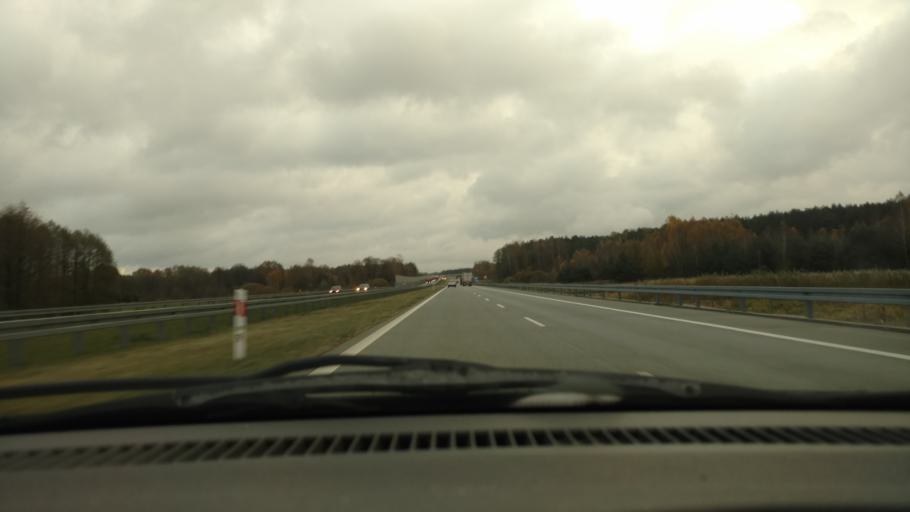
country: PL
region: Lodz Voivodeship
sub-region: Powiat pabianicki
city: Ksawerow
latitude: 51.6312
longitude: 19.4186
